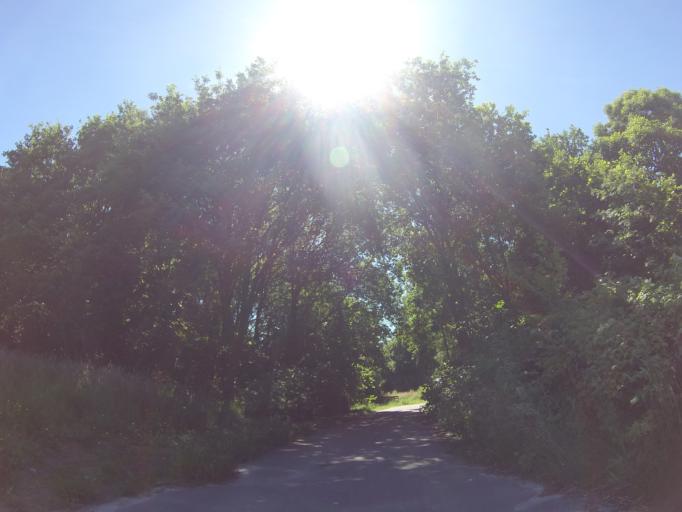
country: NL
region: Drenthe
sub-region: Gemeente Assen
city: Assen
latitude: 52.9711
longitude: 6.5655
